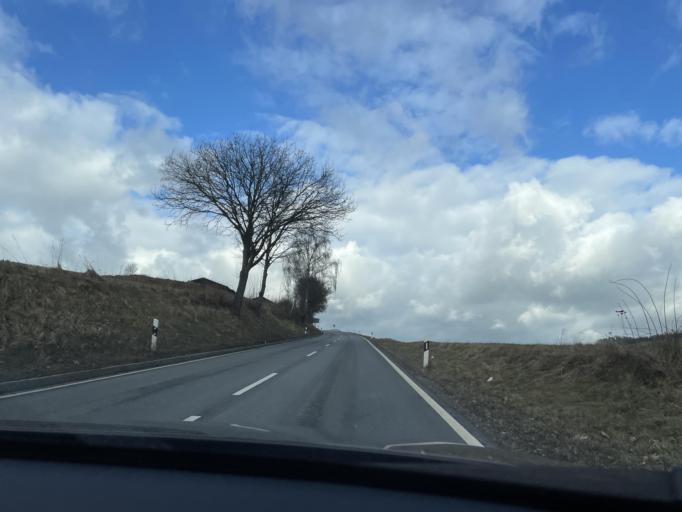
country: DE
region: Bavaria
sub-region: Upper Palatinate
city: Runding
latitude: 49.2036
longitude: 12.7757
